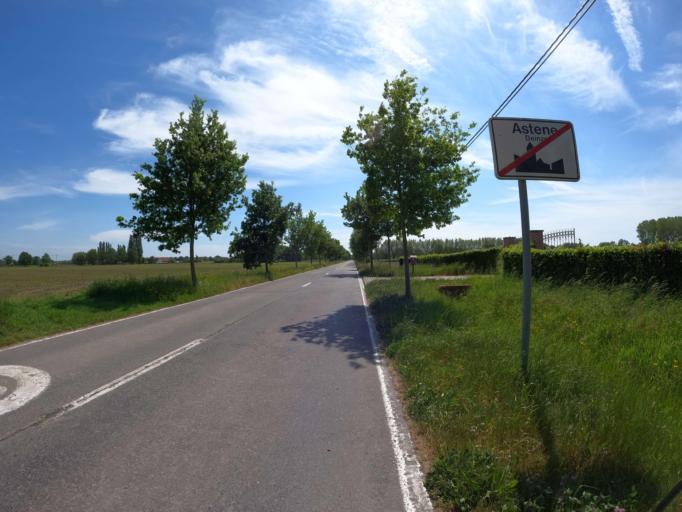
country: BE
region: Flanders
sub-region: Provincie Oost-Vlaanderen
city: Nazareth
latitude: 50.9742
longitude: 3.5722
